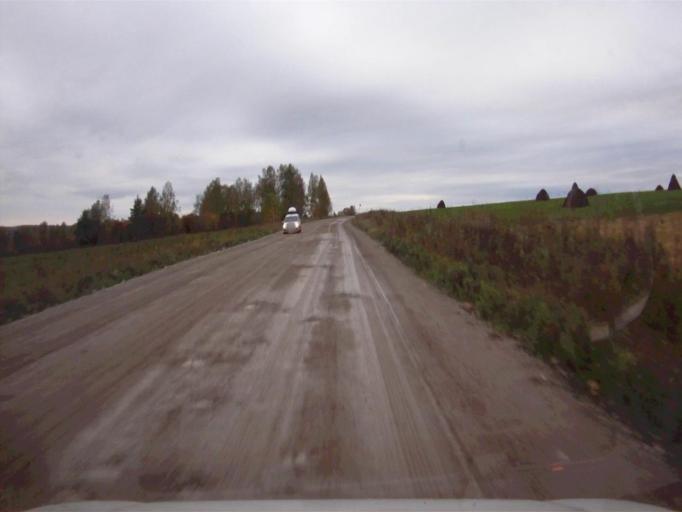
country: RU
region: Sverdlovsk
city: Mikhaylovsk
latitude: 56.1769
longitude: 59.2095
